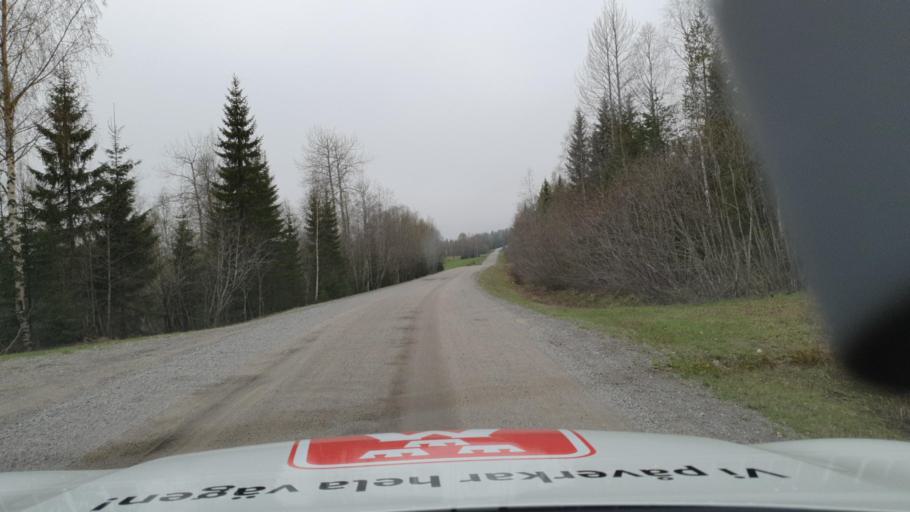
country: SE
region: Vaesterbotten
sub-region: Nordmalings Kommun
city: Nordmaling
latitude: 63.7652
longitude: 19.4440
